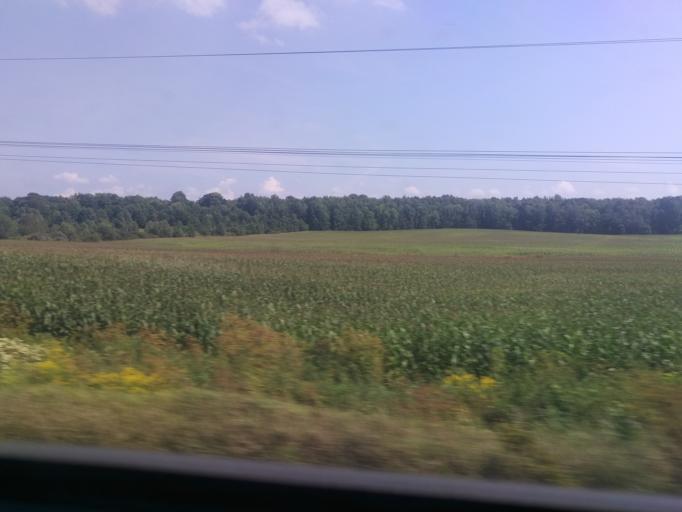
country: CA
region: Ontario
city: Brockville
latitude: 44.5329
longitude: -75.8194
